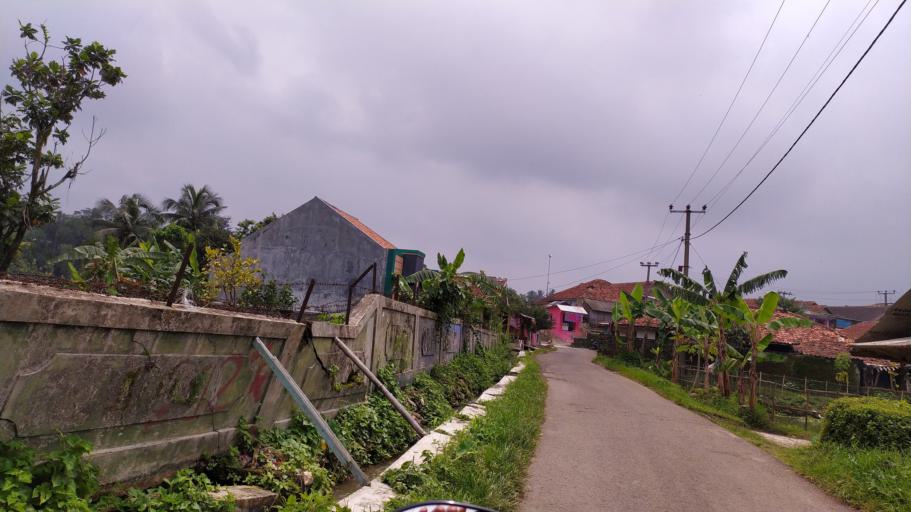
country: ID
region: West Java
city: Ciampea
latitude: -6.6178
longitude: 106.7109
